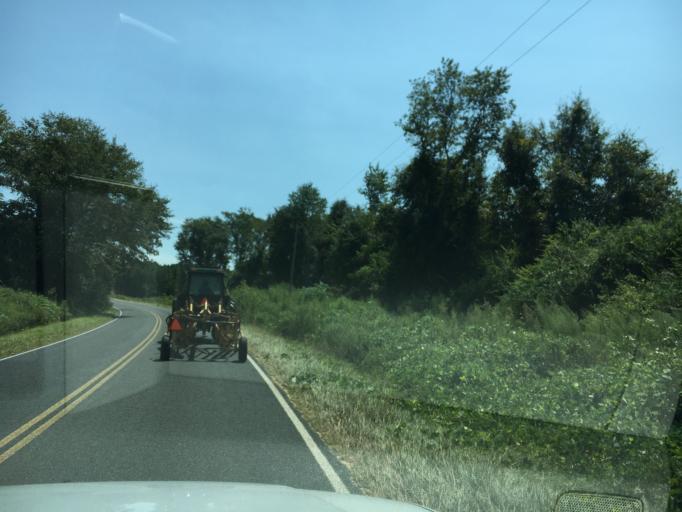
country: US
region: South Carolina
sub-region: Lexington County
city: Batesburg
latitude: 33.8021
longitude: -81.6454
